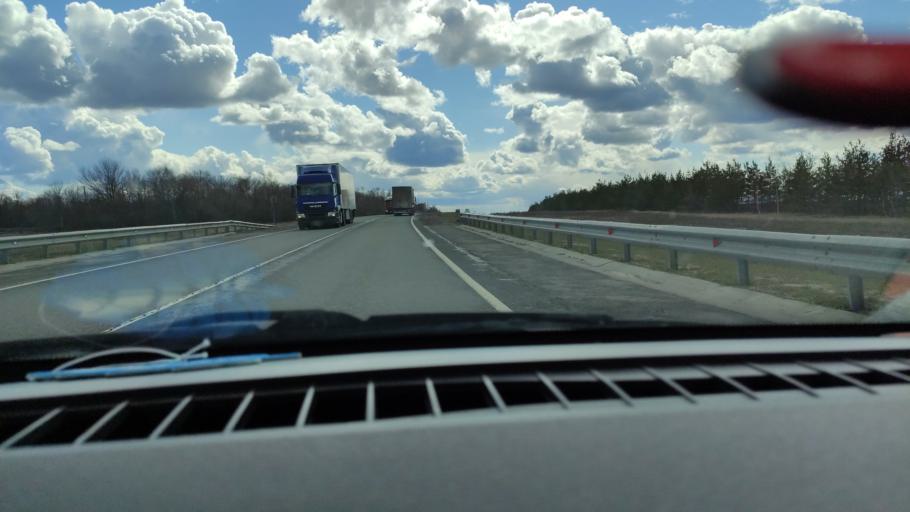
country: RU
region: Samara
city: Syzran'
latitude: 52.8704
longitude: 48.2837
